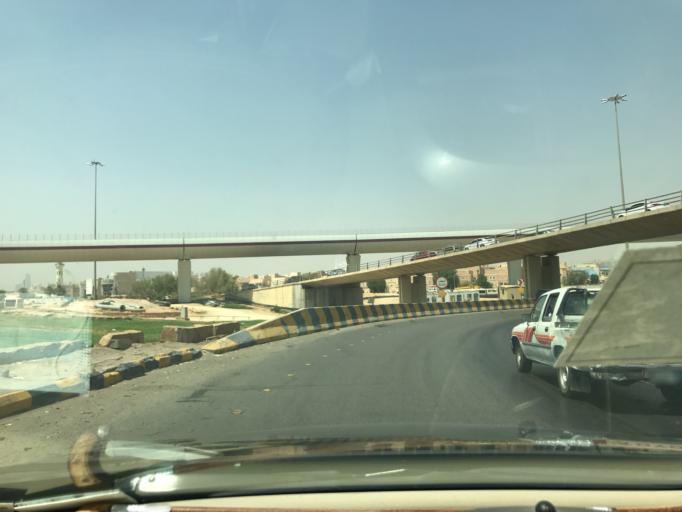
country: SA
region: Ar Riyad
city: Riyadh
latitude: 24.7922
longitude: 46.7212
